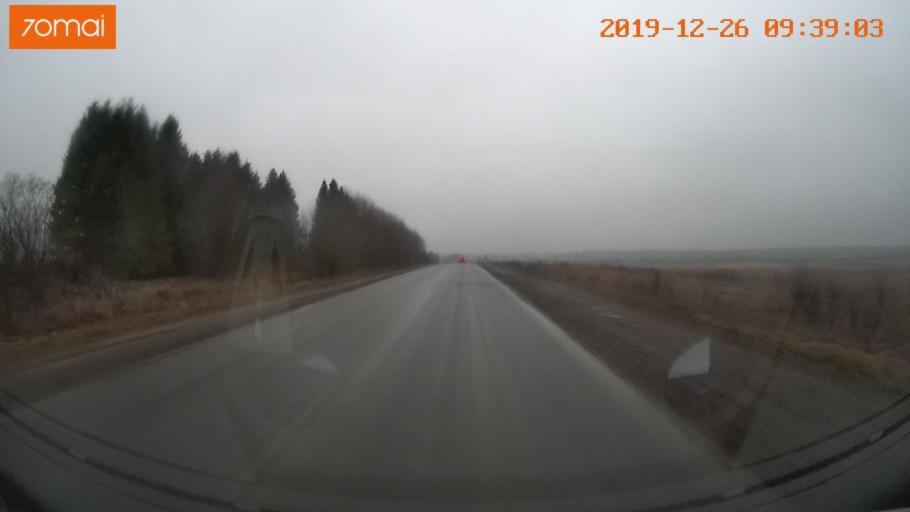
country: RU
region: Vologda
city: Vologda
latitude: 59.1505
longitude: 40.0319
